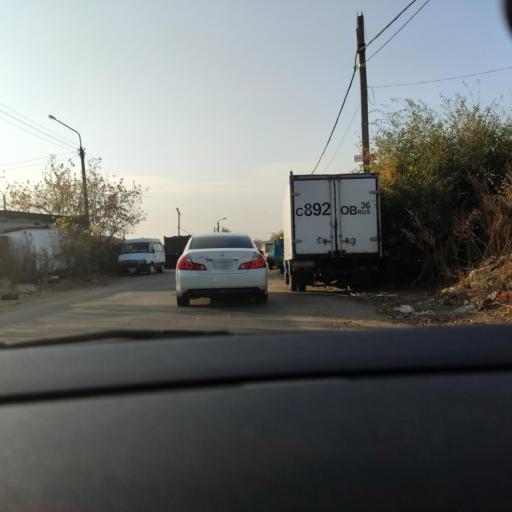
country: RU
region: Voronezj
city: Podgornoye
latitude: 51.7004
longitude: 39.1298
